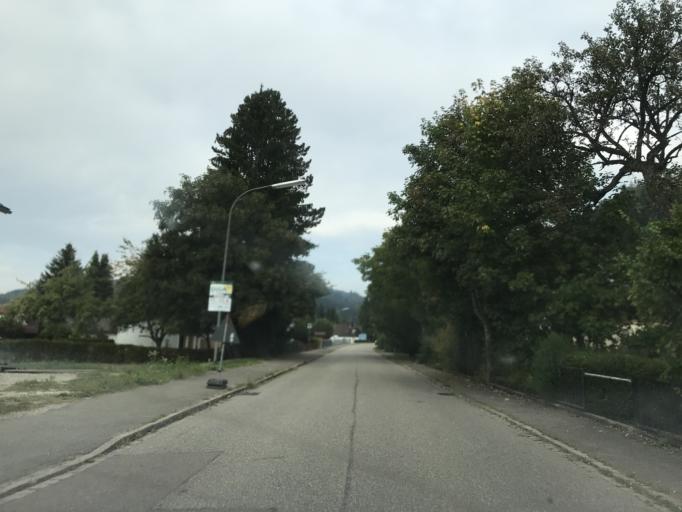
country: DE
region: Baden-Wuerttemberg
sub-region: Freiburg Region
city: Wehr
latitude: 47.6356
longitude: 7.9111
